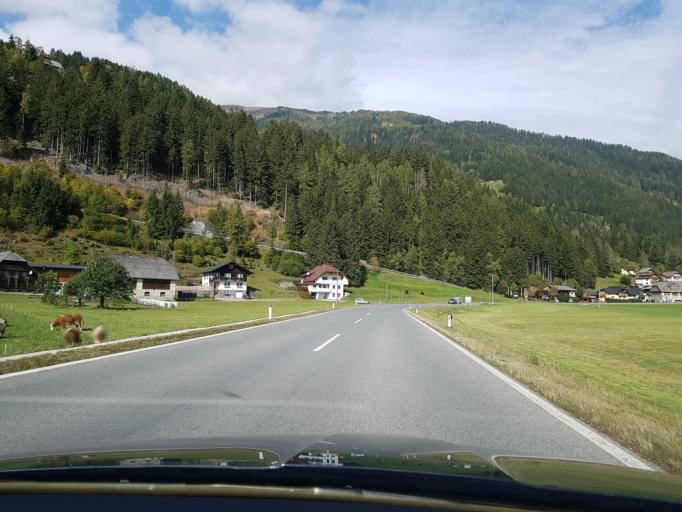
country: AT
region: Carinthia
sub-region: Politischer Bezirk Spittal an der Drau
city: Kleinkirchheim
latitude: 46.8254
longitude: 13.8602
